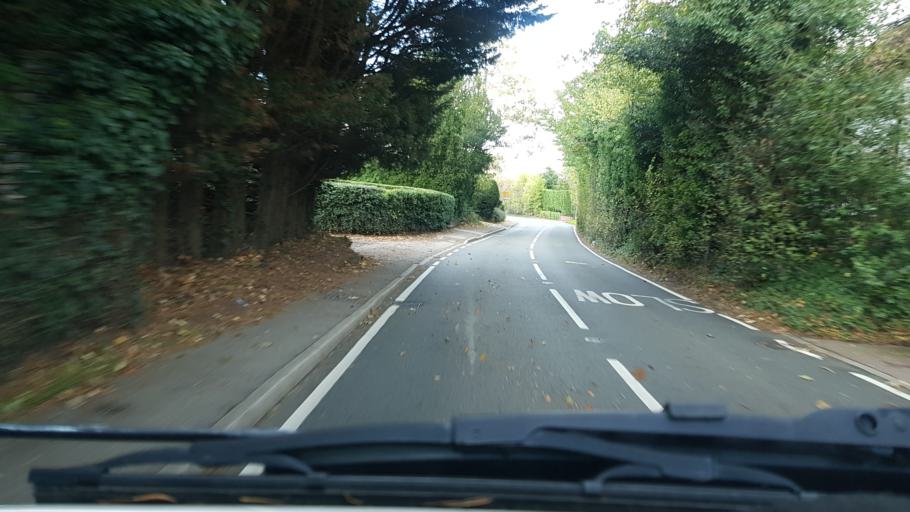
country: GB
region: England
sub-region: Surrey
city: Send
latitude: 51.2586
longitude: -0.5032
